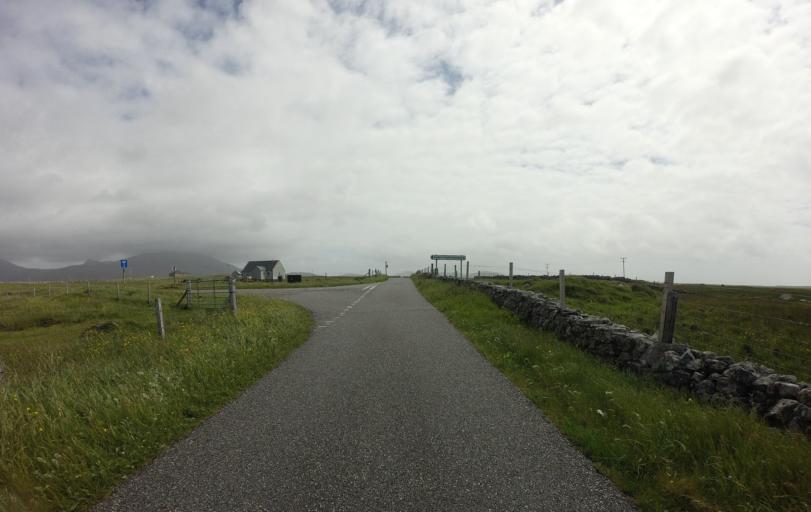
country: GB
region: Scotland
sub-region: Eilean Siar
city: Isle of South Uist
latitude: 57.2772
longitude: -7.4119
